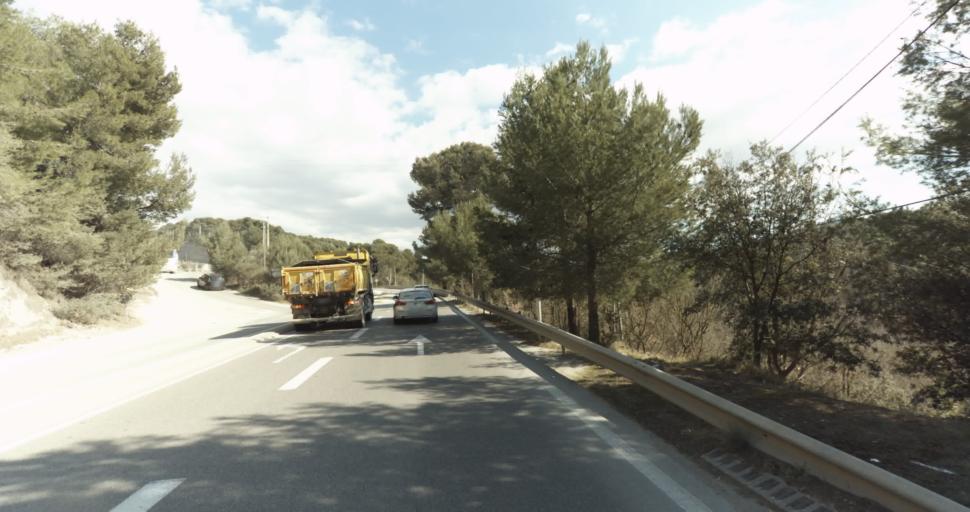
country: FR
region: Provence-Alpes-Cote d'Azur
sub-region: Departement des Bouches-du-Rhone
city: Gardanne
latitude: 43.4518
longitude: 5.4957
